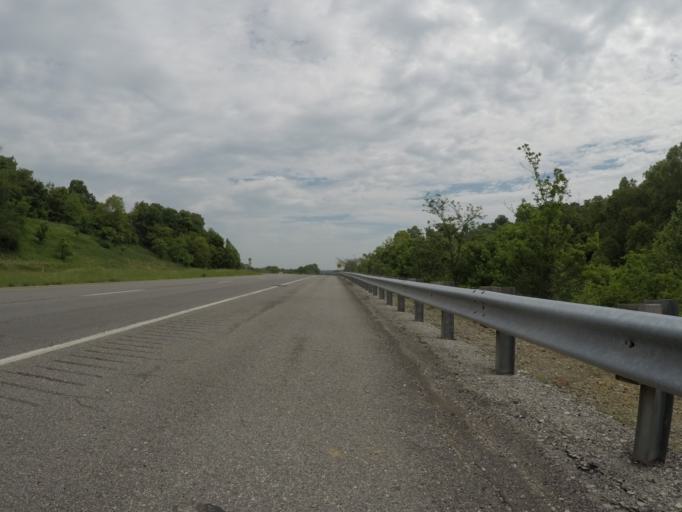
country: US
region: West Virginia
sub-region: Wayne County
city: Kenova
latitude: 38.3790
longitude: -82.5835
